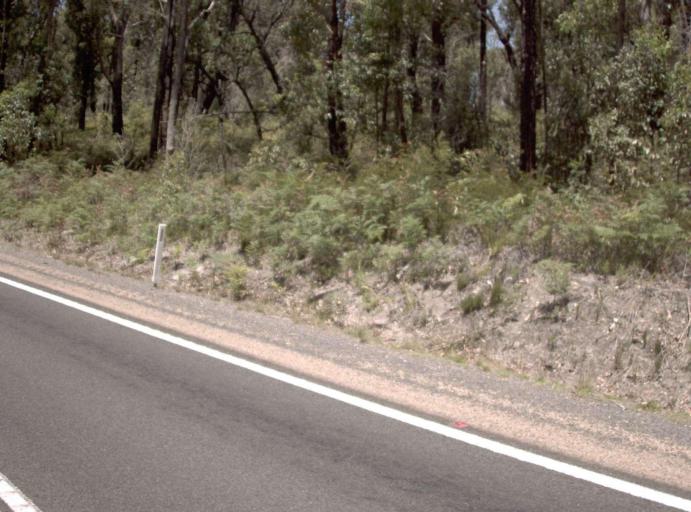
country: AU
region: Victoria
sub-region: East Gippsland
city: Lakes Entrance
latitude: -37.6960
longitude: 148.7380
